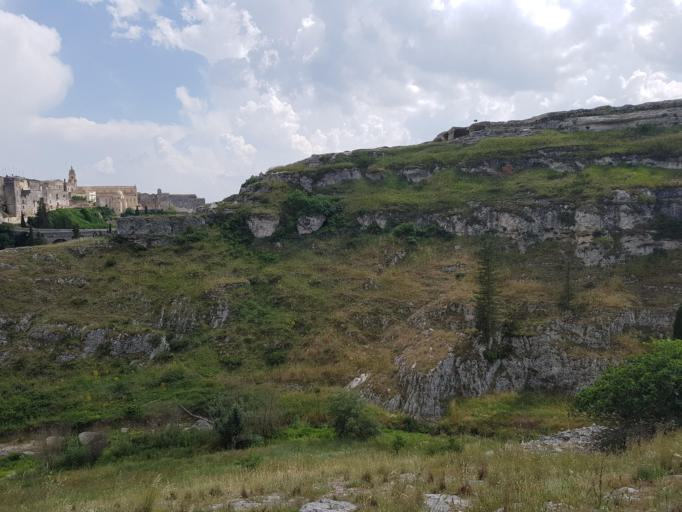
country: IT
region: Apulia
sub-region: Provincia di Bari
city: Gravina in Puglia
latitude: 40.8222
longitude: 16.4125
